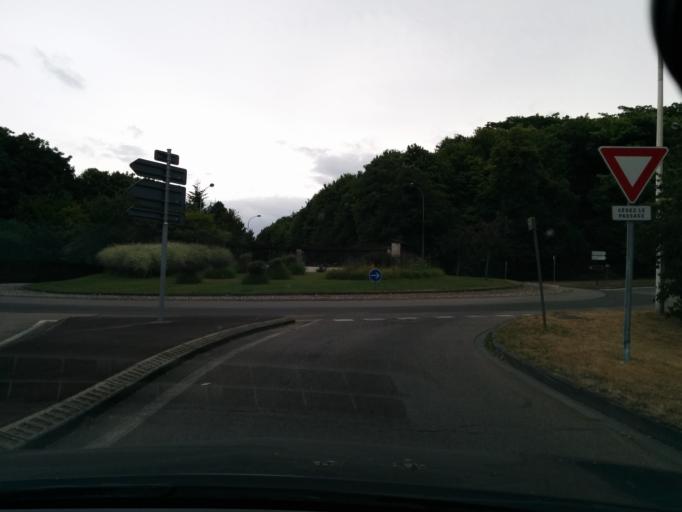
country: FR
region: Haute-Normandie
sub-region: Departement de l'Eure
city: Vernon
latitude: 49.0798
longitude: 1.5051
